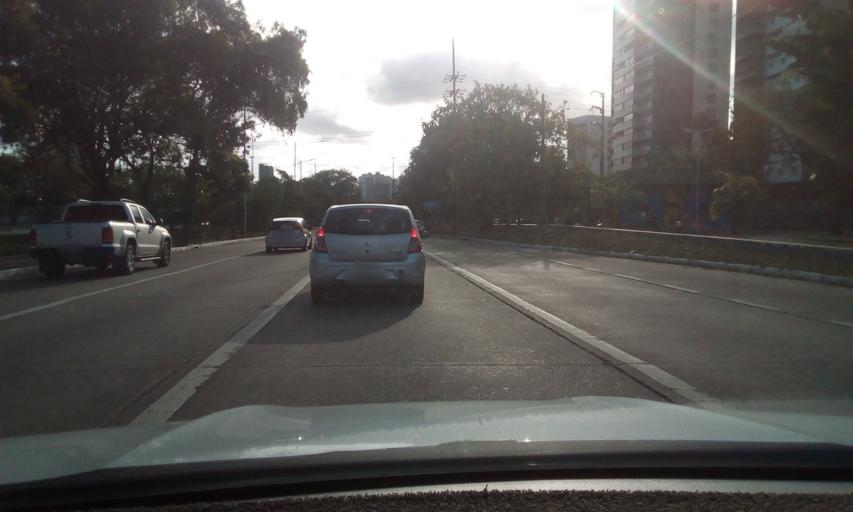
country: BR
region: Pernambuco
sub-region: Recife
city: Recife
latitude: -8.0414
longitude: -34.8828
